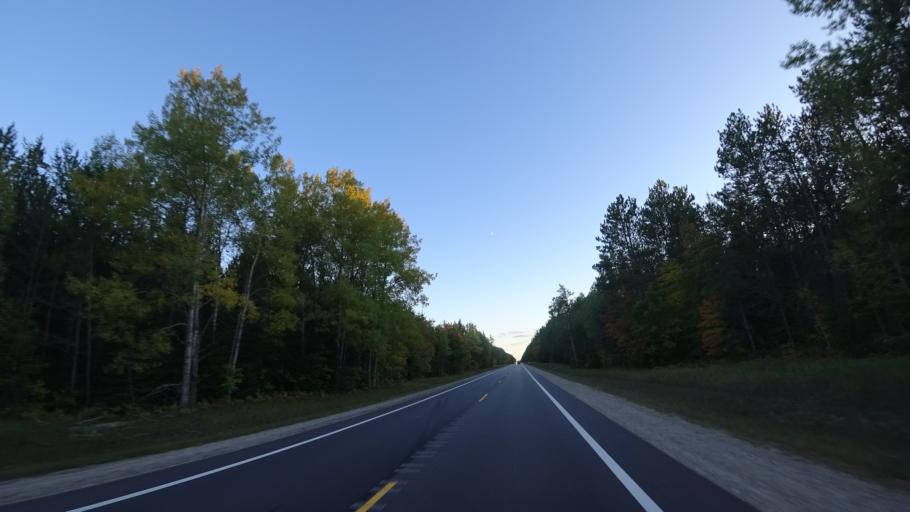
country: US
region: Michigan
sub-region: Luce County
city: Newberry
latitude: 46.3067
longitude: -85.0094
